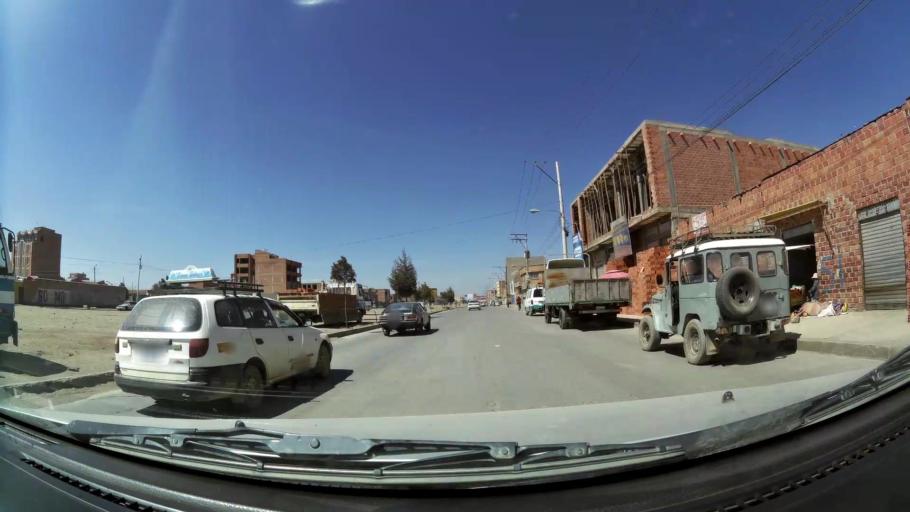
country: BO
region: La Paz
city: La Paz
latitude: -16.5435
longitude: -68.1977
